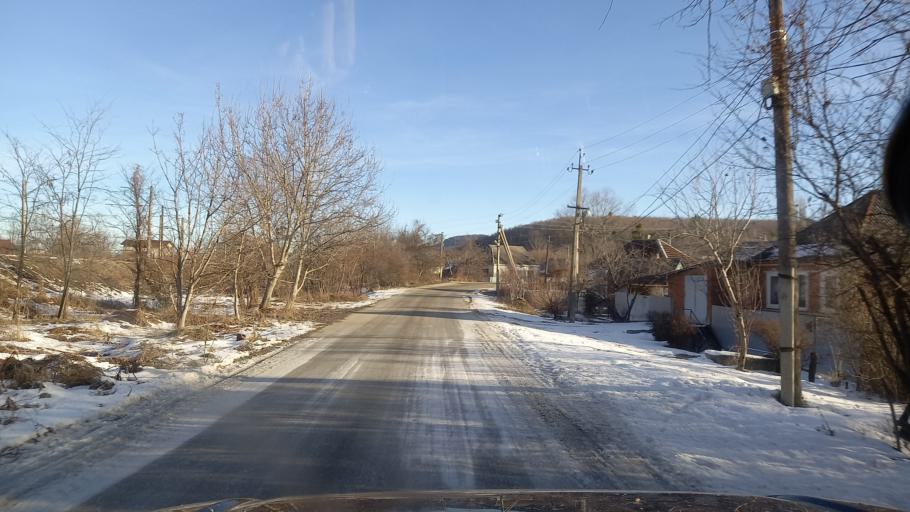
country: RU
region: Adygeya
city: Kamennomostskiy
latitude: 44.2946
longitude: 40.1874
